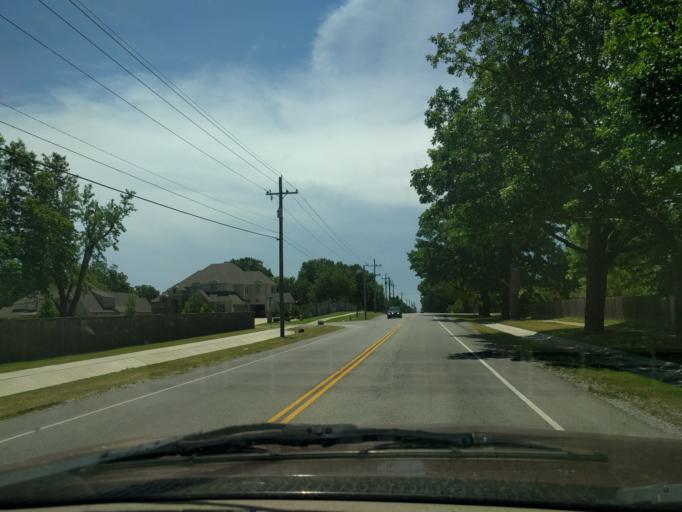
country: US
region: Oklahoma
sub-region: Tulsa County
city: Jenks
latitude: 36.0116
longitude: -95.9222
